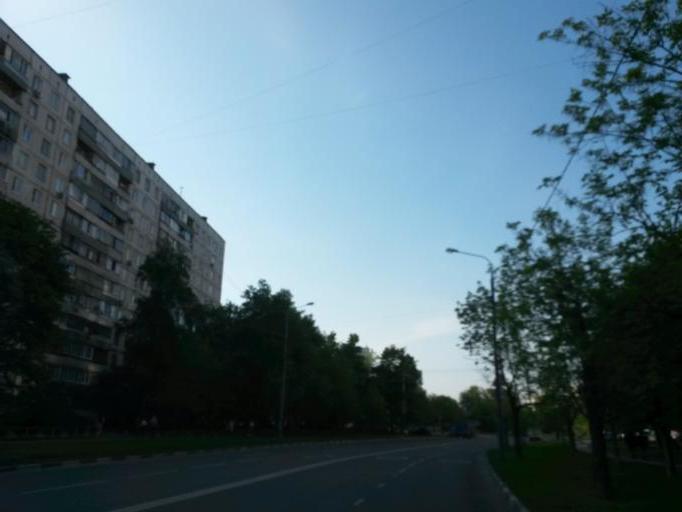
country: RU
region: Moskovskaya
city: Biryulevo Zapadnoye
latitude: 55.5878
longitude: 37.6456
